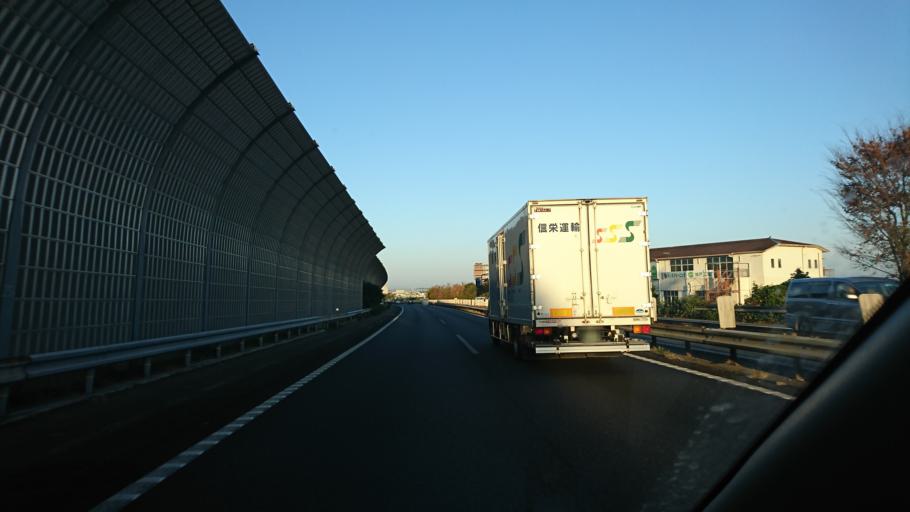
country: JP
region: Hyogo
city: Akashi
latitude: 34.7144
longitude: 134.9345
